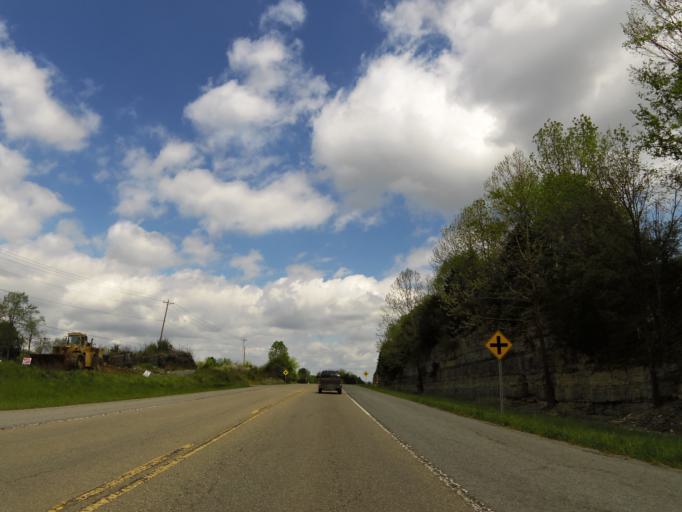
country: US
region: Kentucky
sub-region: Bell County
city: Middlesboro
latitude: 36.5281
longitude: -83.7370
